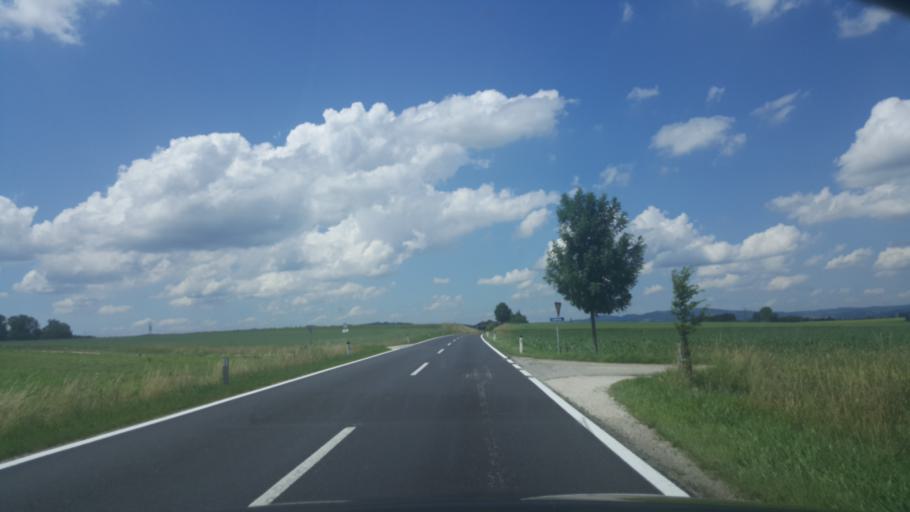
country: AT
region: Upper Austria
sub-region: Politischer Bezirk Vocklabruck
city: Gampern
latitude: 47.9721
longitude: 13.5643
